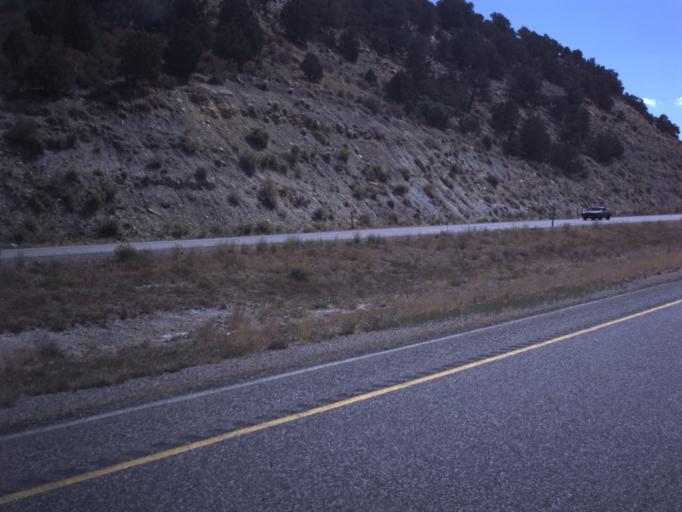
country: US
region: Utah
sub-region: Sevier County
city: Salina
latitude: 38.8231
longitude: -111.5396
